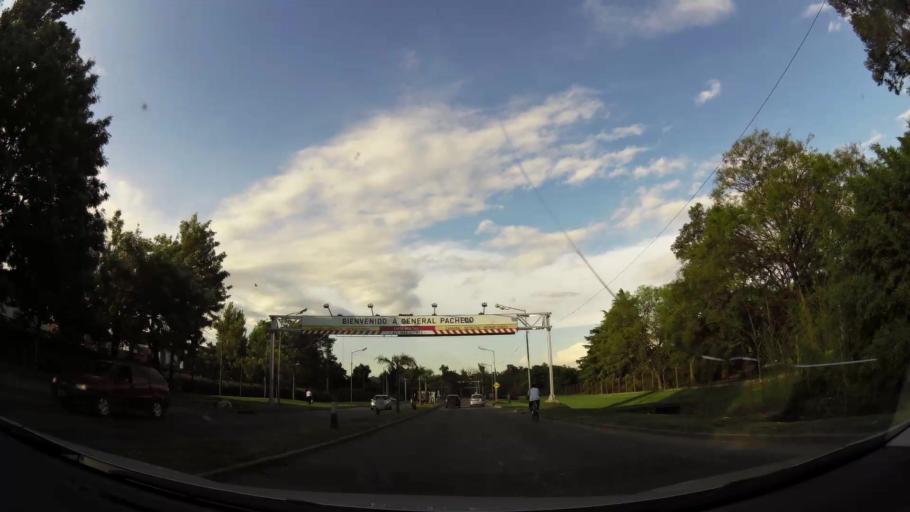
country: AR
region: Buenos Aires
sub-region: Partido de Tigre
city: Tigre
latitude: -34.4707
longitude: -58.6247
